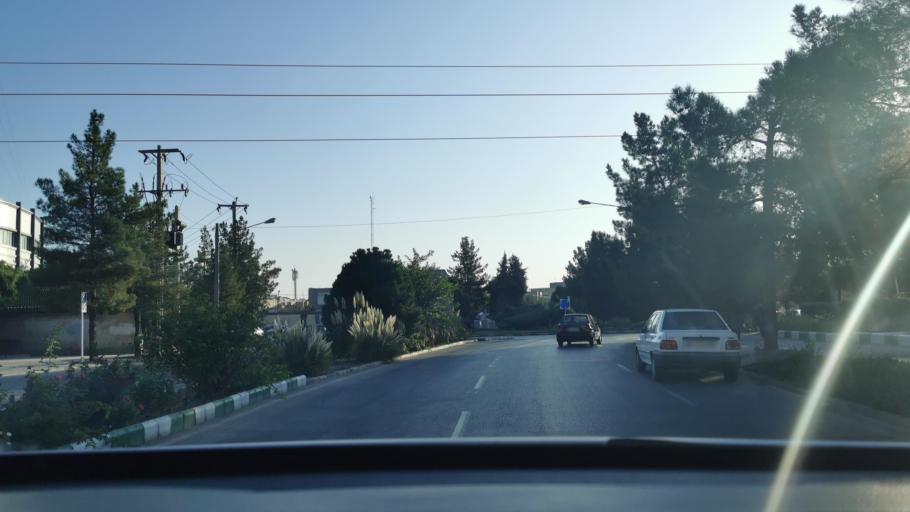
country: IR
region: Razavi Khorasan
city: Mashhad
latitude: 36.3618
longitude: 59.5143
